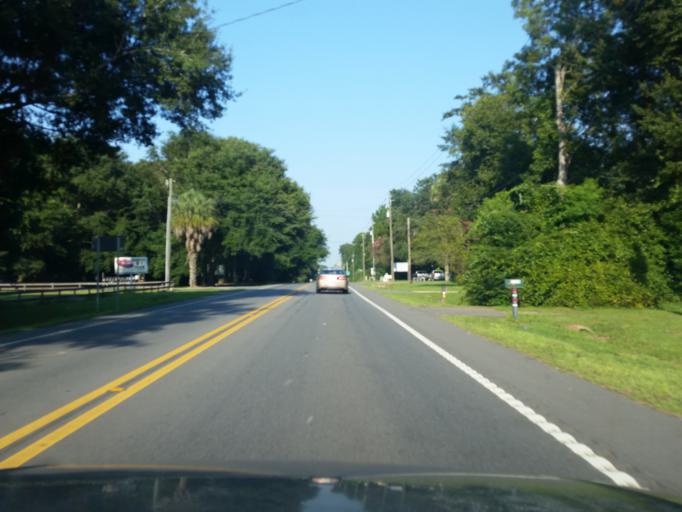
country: US
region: Alabama
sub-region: Baldwin County
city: Foley
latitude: 30.4068
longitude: -87.6599
